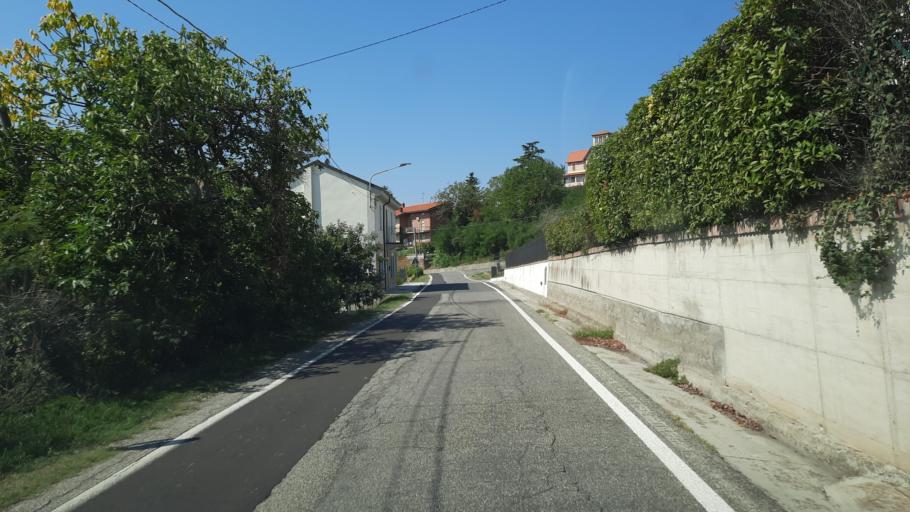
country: IT
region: Piedmont
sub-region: Provincia di Alessandria
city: Gabiano
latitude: 45.1584
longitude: 8.1978
